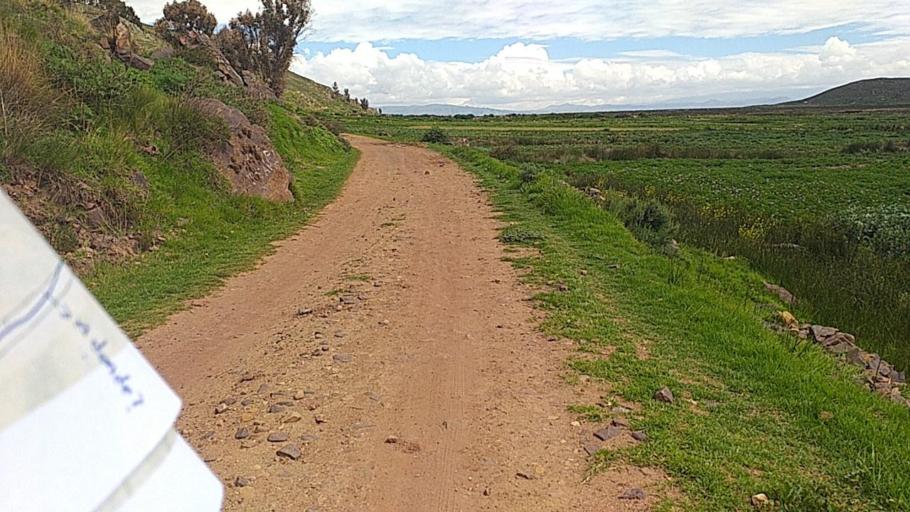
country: BO
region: La Paz
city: Batallas
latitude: -16.3435
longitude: -68.6348
